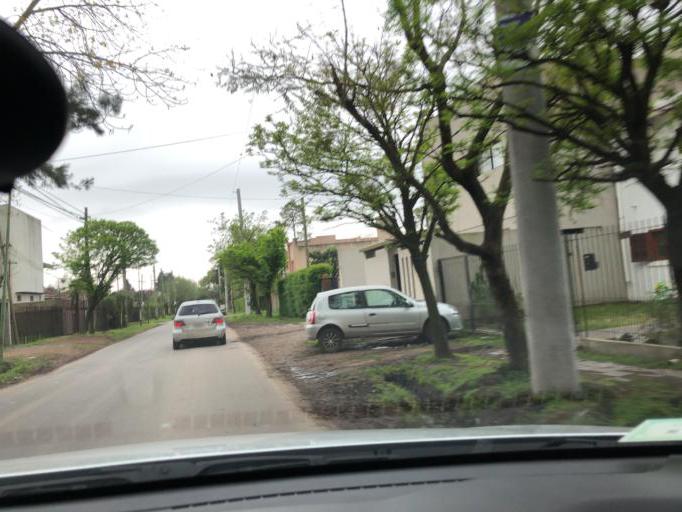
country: AR
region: Buenos Aires
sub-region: Partido de La Plata
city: La Plata
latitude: -34.8939
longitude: -58.0654
